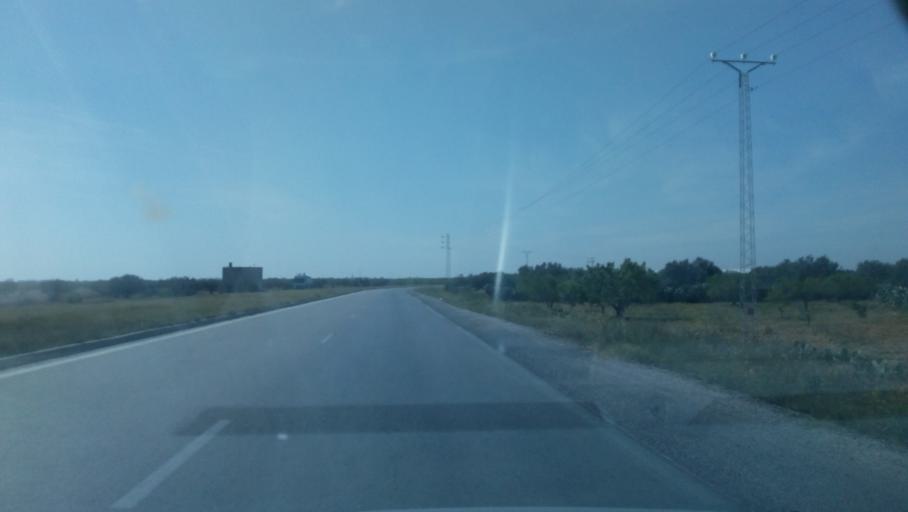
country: TN
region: Safaqis
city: Al Qarmadah
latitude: 34.8614
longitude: 10.7983
